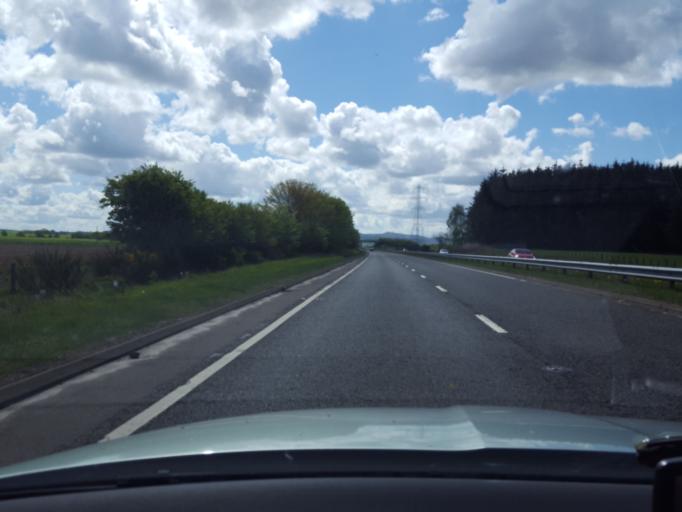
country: GB
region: Scotland
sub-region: Angus
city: Forfar
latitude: 56.6610
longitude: -2.9139
